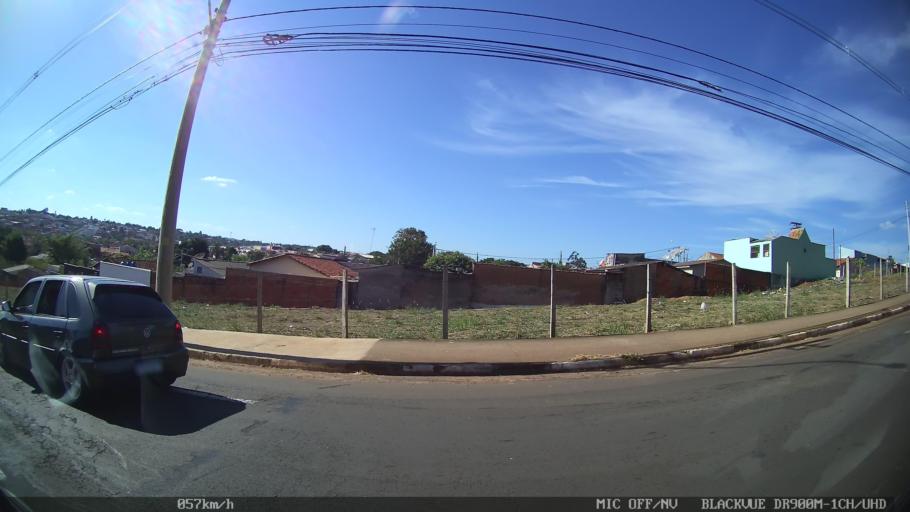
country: BR
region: Sao Paulo
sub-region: Franca
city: Franca
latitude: -20.4937
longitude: -47.4271
